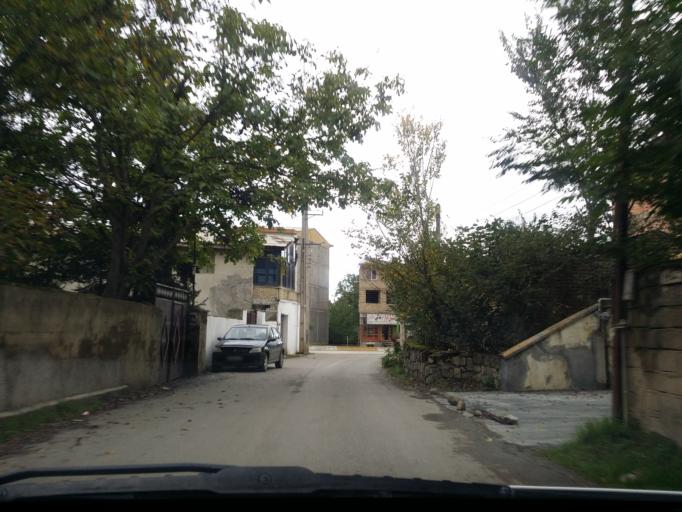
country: IR
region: Mazandaran
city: `Abbasabad
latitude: 36.5076
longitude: 51.1904
